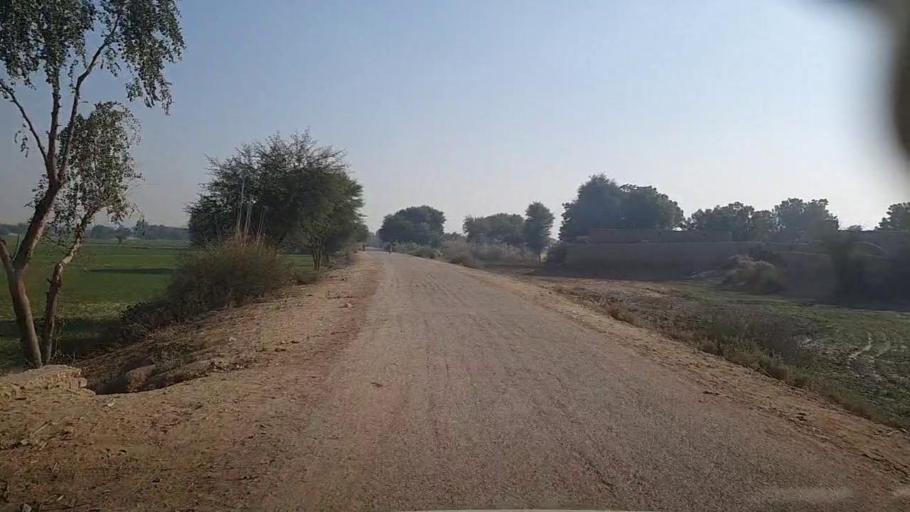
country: PK
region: Sindh
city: Kandiari
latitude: 26.8154
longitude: 68.4955
